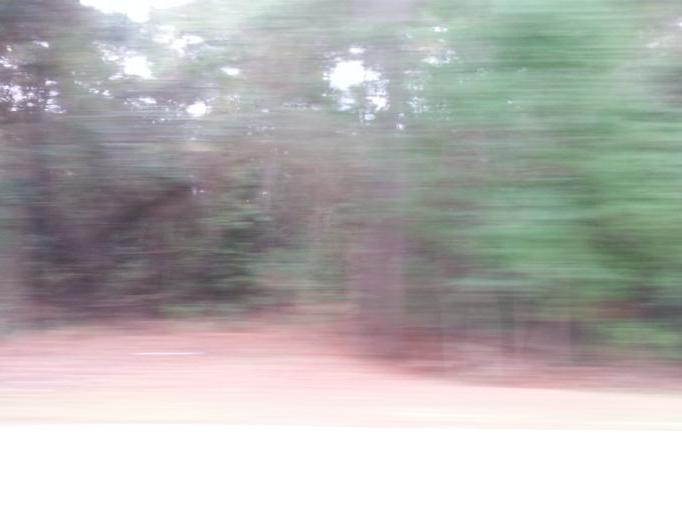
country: US
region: Alabama
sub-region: Baldwin County
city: Point Clear
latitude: 30.4276
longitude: -87.9099
